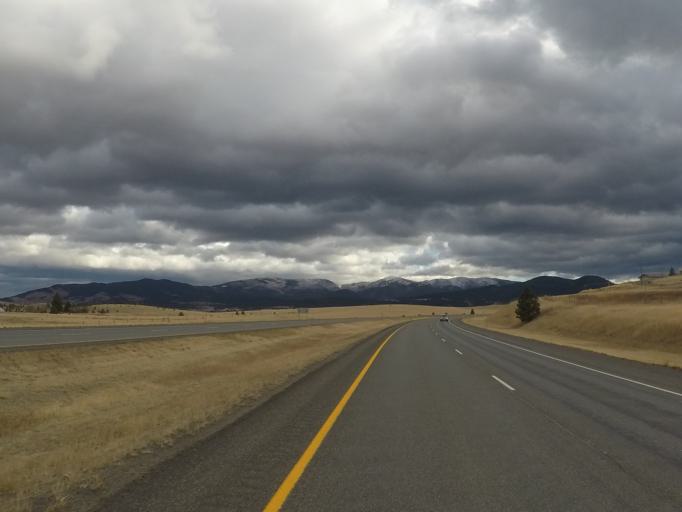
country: US
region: Montana
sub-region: Jefferson County
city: Montana City
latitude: 46.5614
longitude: -111.9556
